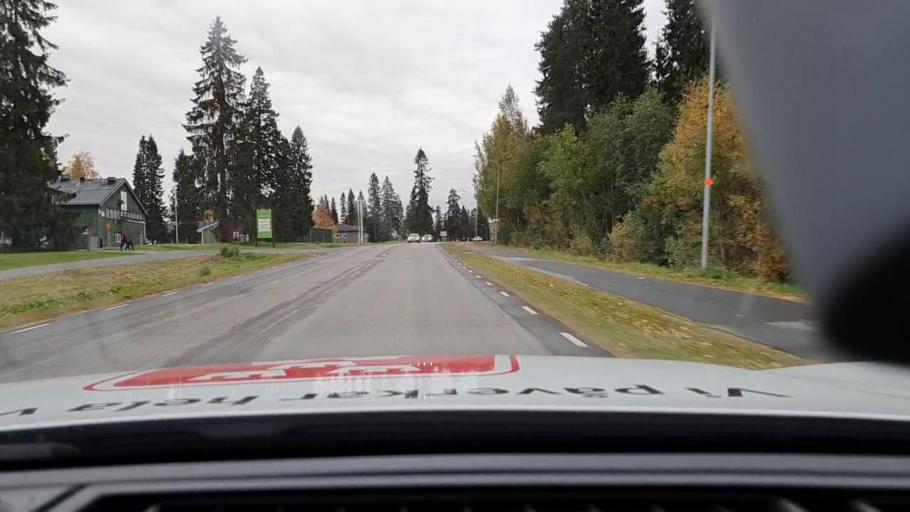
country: SE
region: Norrbotten
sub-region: Bodens Kommun
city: Boden
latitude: 65.8111
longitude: 21.6772
